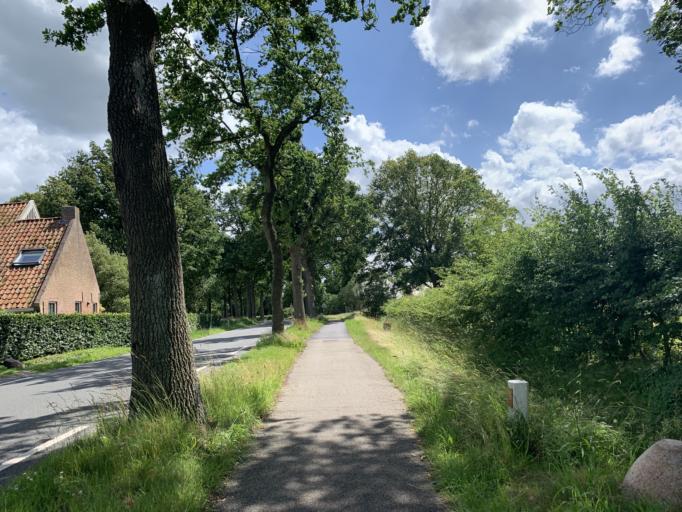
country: NL
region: Groningen
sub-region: Gemeente Haren
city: Haren
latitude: 53.1458
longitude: 6.6485
